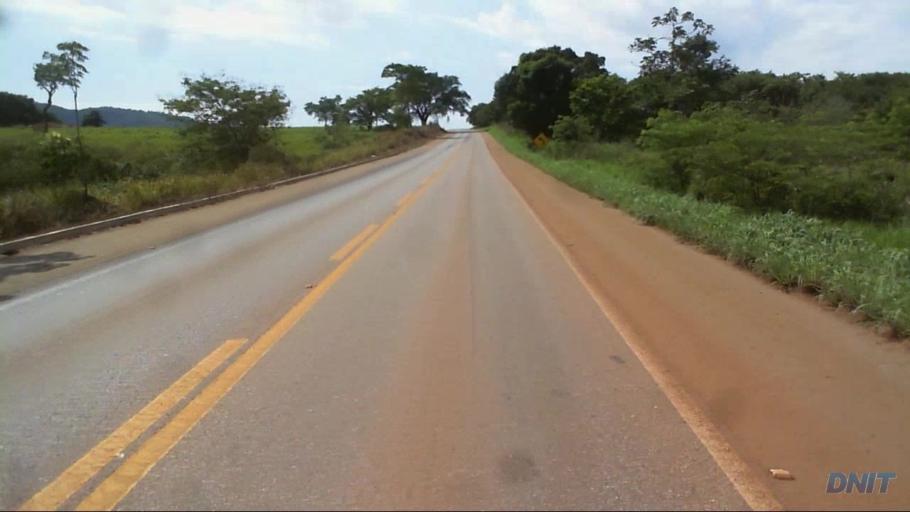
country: BR
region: Goias
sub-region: Barro Alto
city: Barro Alto
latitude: -15.0961
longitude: -48.8534
